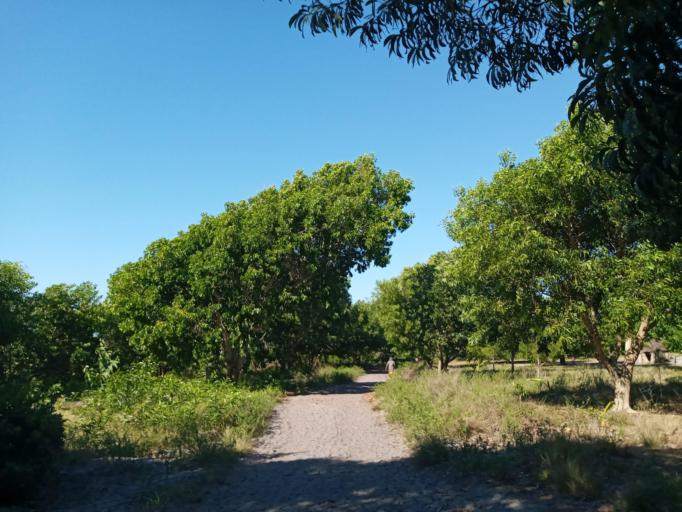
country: MG
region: Anosy
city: Fort Dauphin
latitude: -24.9054
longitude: 47.1012
